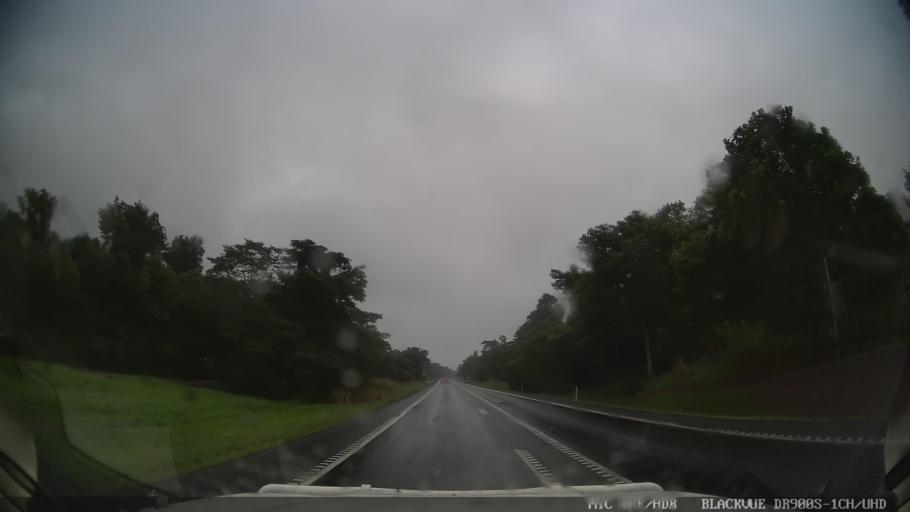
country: AU
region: Queensland
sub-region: Cassowary Coast
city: Innisfail
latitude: -17.8579
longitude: 145.9868
